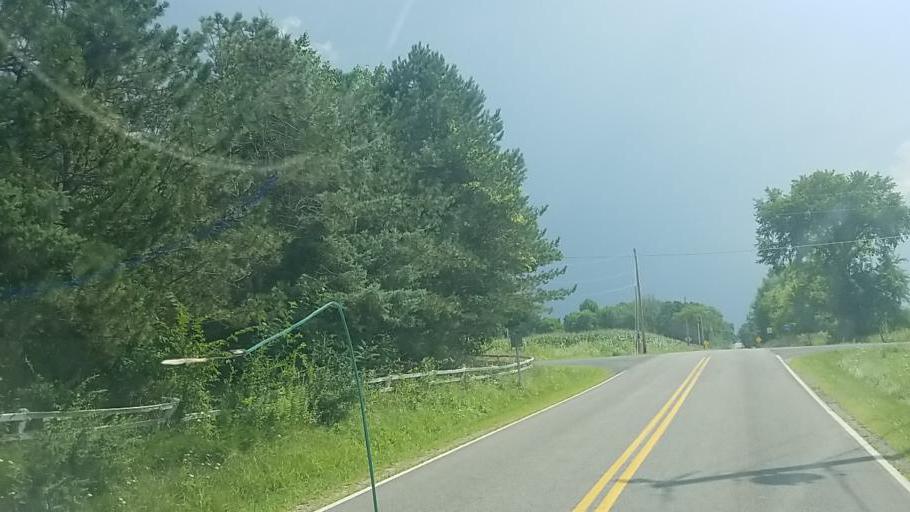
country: US
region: Ohio
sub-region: Medina County
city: Lodi
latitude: 41.0772
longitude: -82.0048
